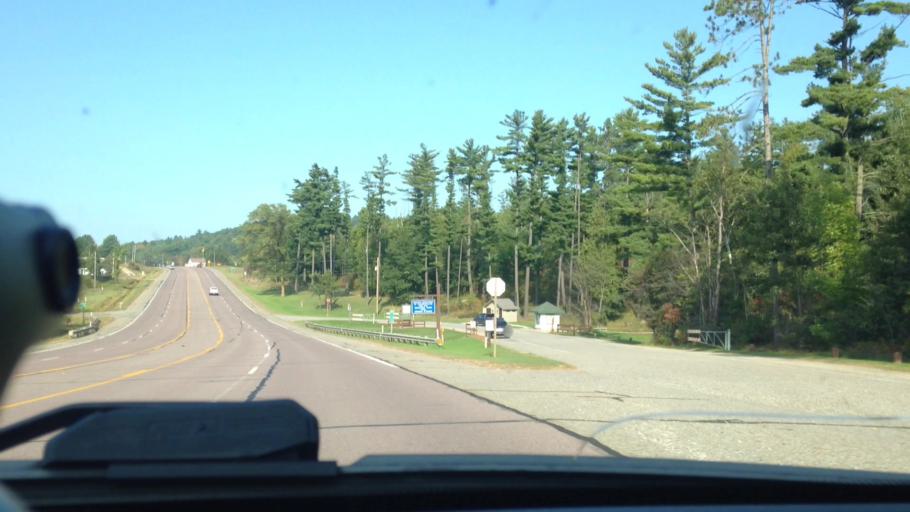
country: US
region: Michigan
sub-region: Dickinson County
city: Quinnesec
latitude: 45.8055
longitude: -87.9772
